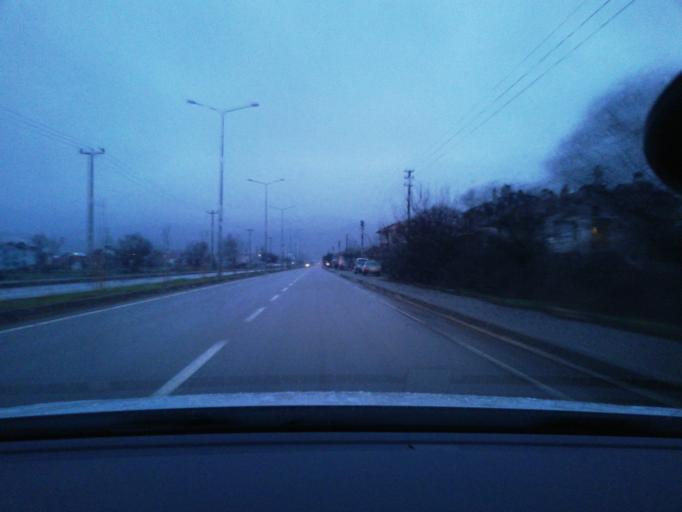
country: TR
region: Bolu
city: Bolu
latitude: 40.6980
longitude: 31.6188
